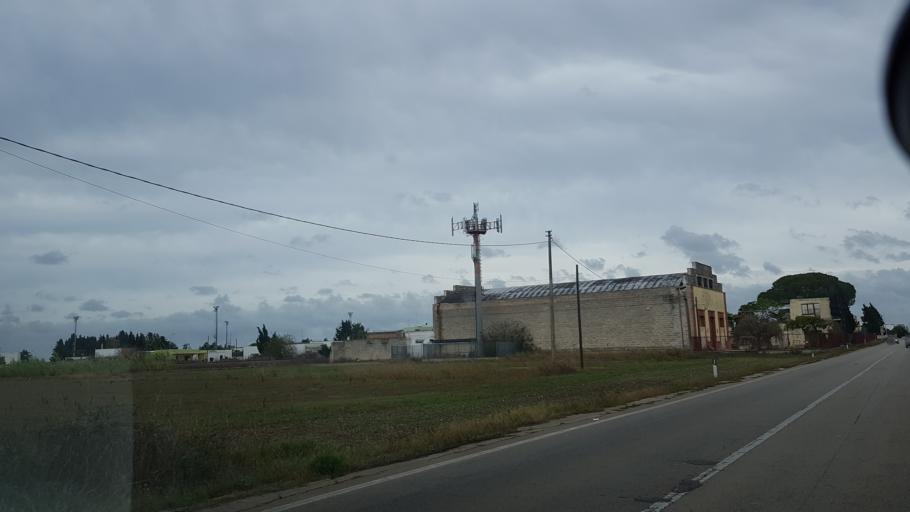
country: IT
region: Apulia
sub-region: Provincia di Lecce
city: Guagnano
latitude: 40.3999
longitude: 17.9383
